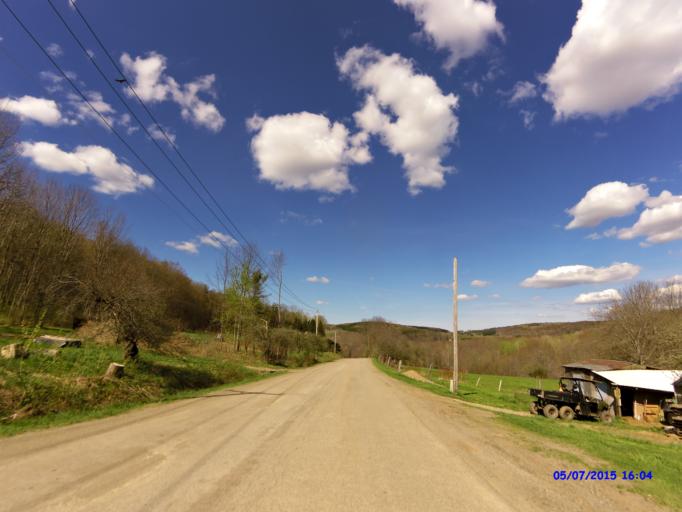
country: US
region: New York
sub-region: Cattaraugus County
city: Franklinville
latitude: 42.2995
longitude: -78.6143
